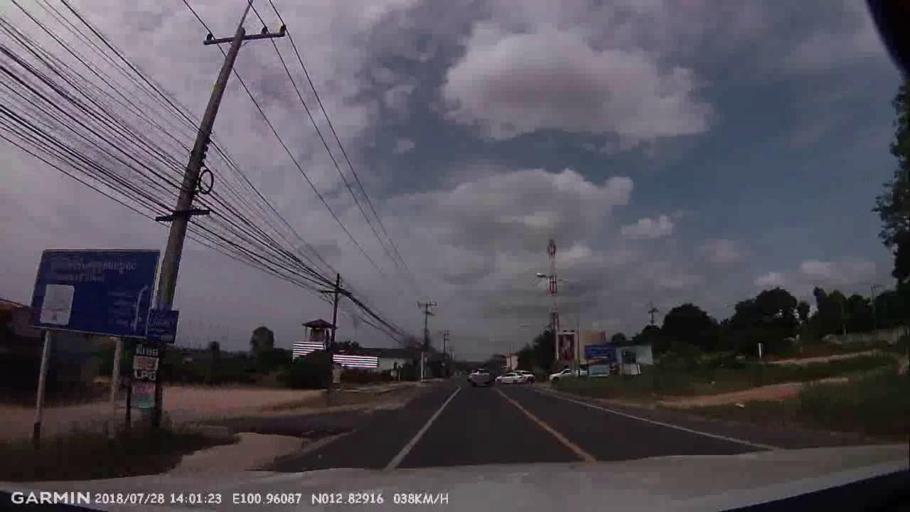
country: TH
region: Chon Buri
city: Phatthaya
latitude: 12.8292
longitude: 100.9610
